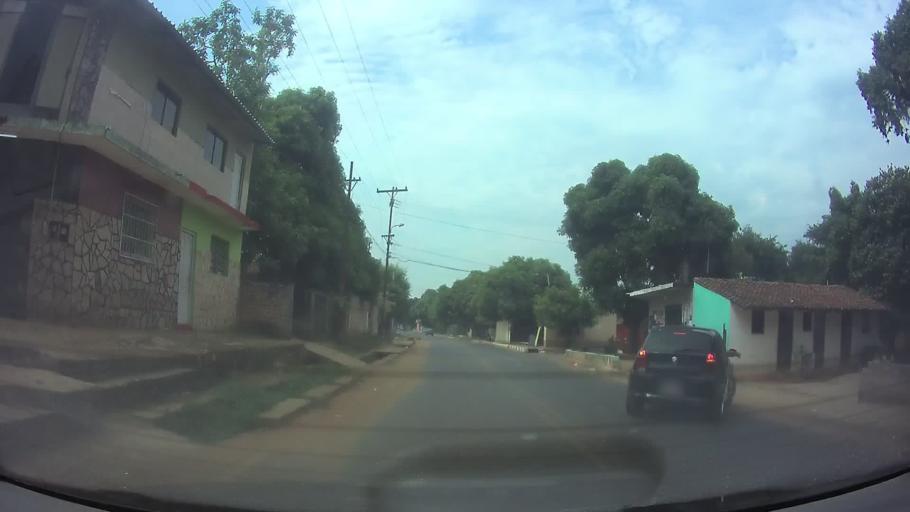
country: PY
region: Central
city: Fernando de la Mora
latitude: -25.2937
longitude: -57.5117
